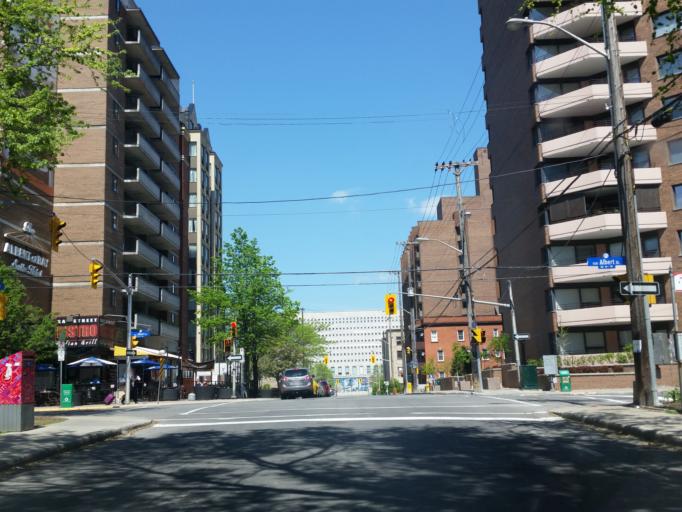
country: CA
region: Ontario
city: Ottawa
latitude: 45.4173
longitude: -75.7058
